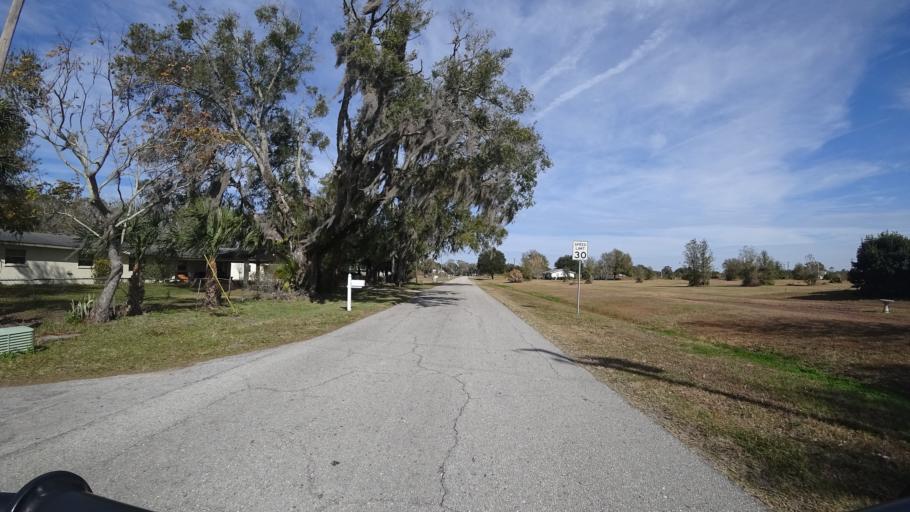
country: US
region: Florida
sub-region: Manatee County
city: Ellenton
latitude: 27.5799
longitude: -82.4277
